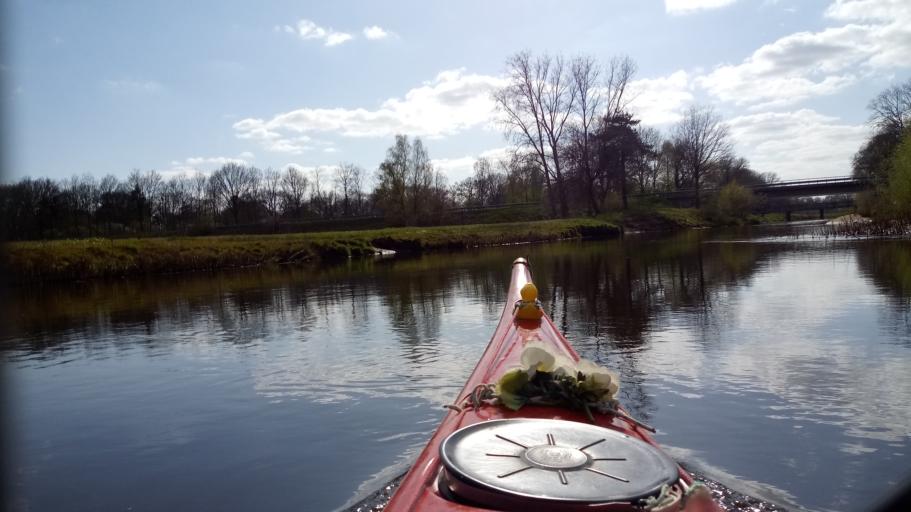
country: NL
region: Overijssel
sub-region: Gemeente Twenterand
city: Den Ham
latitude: 52.4900
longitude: 6.4275
